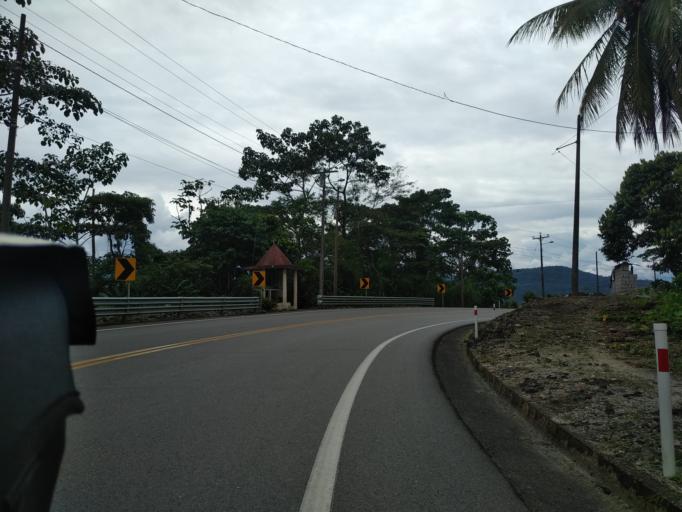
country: EC
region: Napo
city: Tena
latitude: -1.2436
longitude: -77.8778
